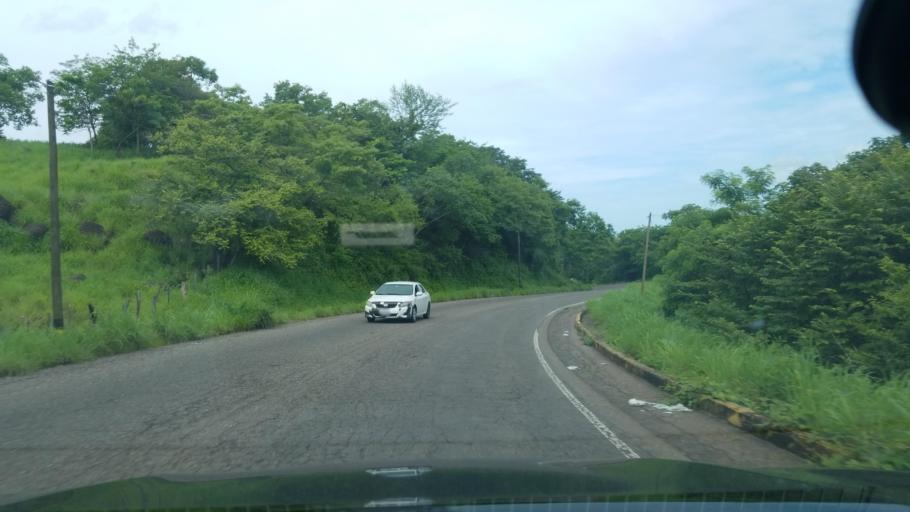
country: HN
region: Choluteca
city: Corpus
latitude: 13.3744
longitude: -87.0607
